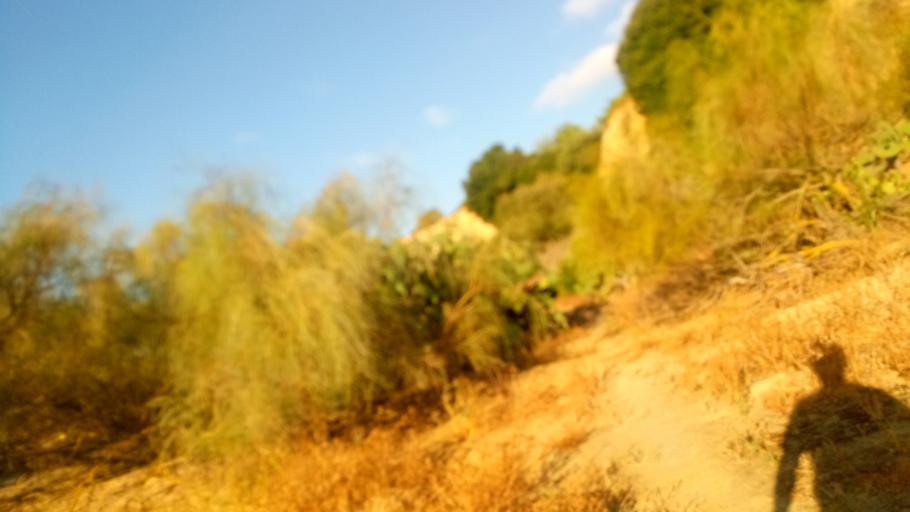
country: PT
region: Faro
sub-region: Tavira
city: Tavira
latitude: 37.1419
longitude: -7.5835
